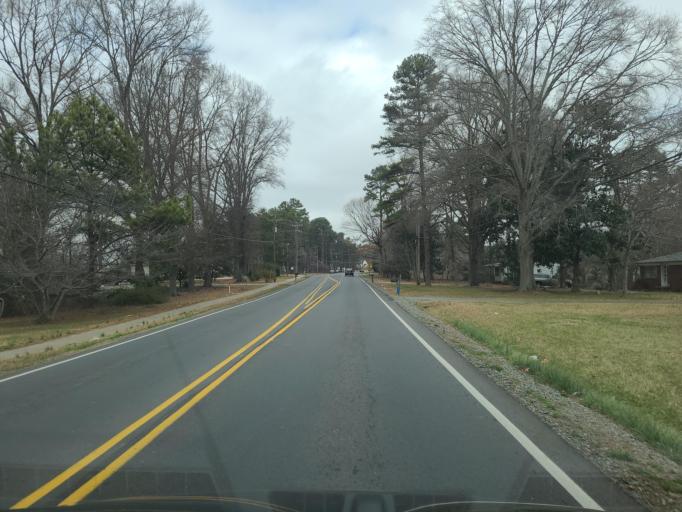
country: US
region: North Carolina
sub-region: Mecklenburg County
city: Mint Hill
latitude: 35.1916
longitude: -80.6866
